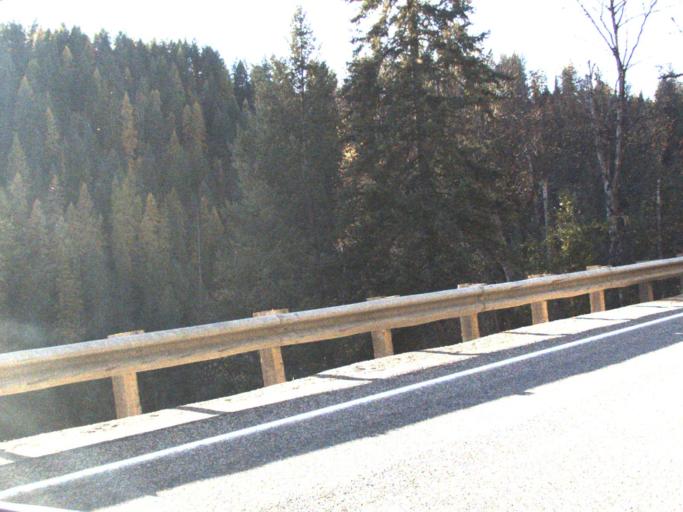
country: CA
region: British Columbia
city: Rossland
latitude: 48.9454
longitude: -117.7919
